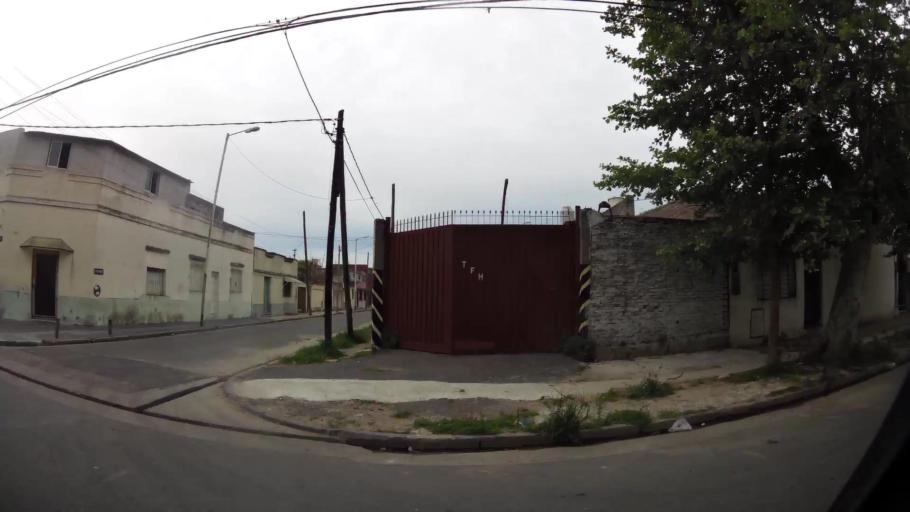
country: AR
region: Buenos Aires
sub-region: Partido de Avellaneda
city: Avellaneda
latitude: -34.6547
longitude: -58.3606
